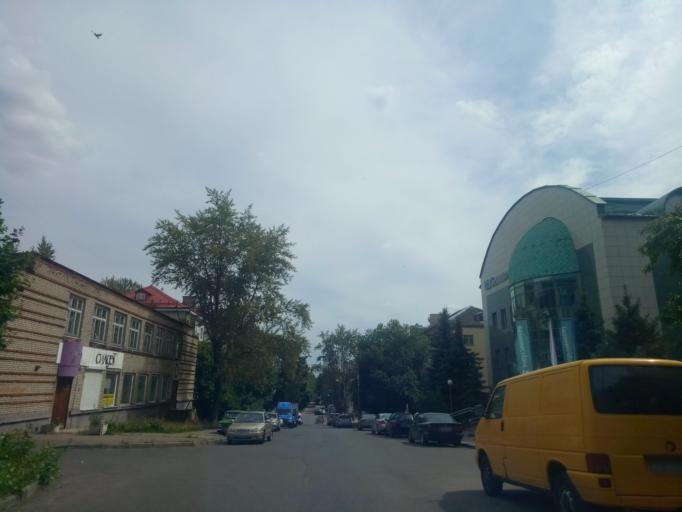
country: BY
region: Minsk
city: Minsk
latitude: 53.8959
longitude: 27.5201
